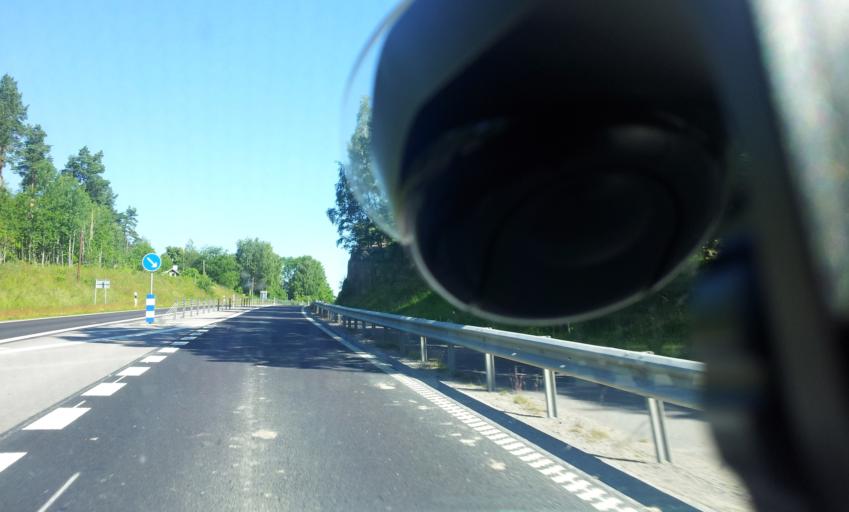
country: SE
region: OEstergoetland
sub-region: Soderkopings Kommun
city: Soederkoeping
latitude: 58.5186
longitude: 16.2872
